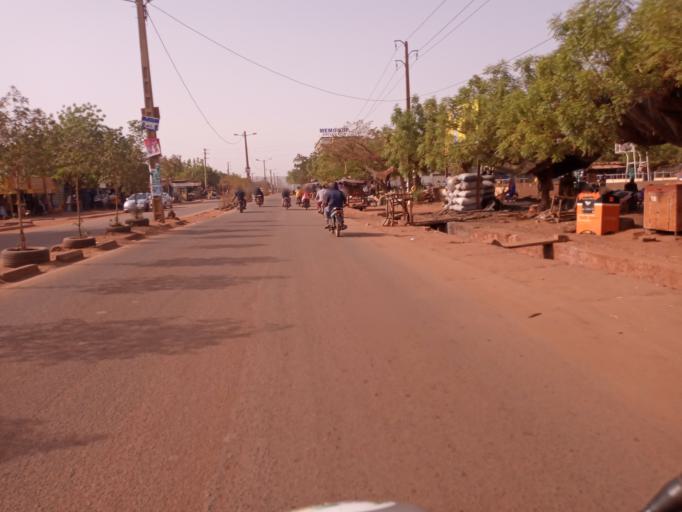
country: ML
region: Bamako
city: Bamako
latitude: 12.6719
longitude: -7.9429
